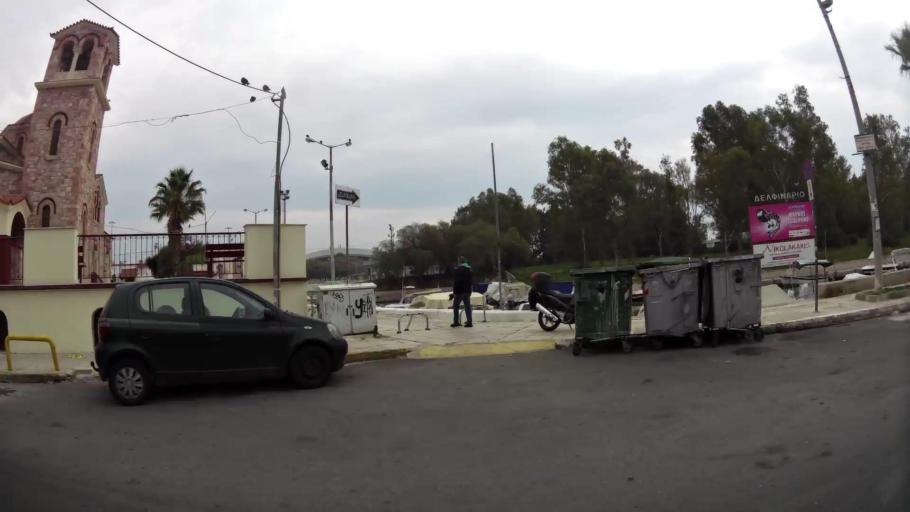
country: GR
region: Attica
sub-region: Nomarchia Athinas
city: Moskhaton
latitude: 37.9431
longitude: 23.6621
